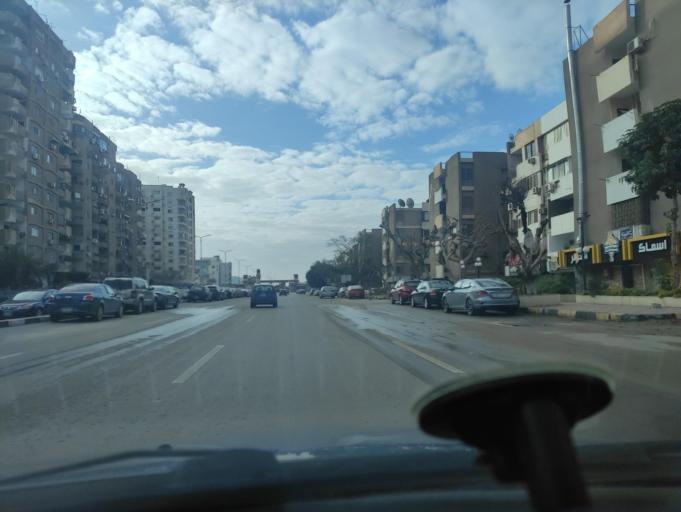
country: EG
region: Muhafazat al Qahirah
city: Cairo
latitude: 30.0482
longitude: 31.3511
